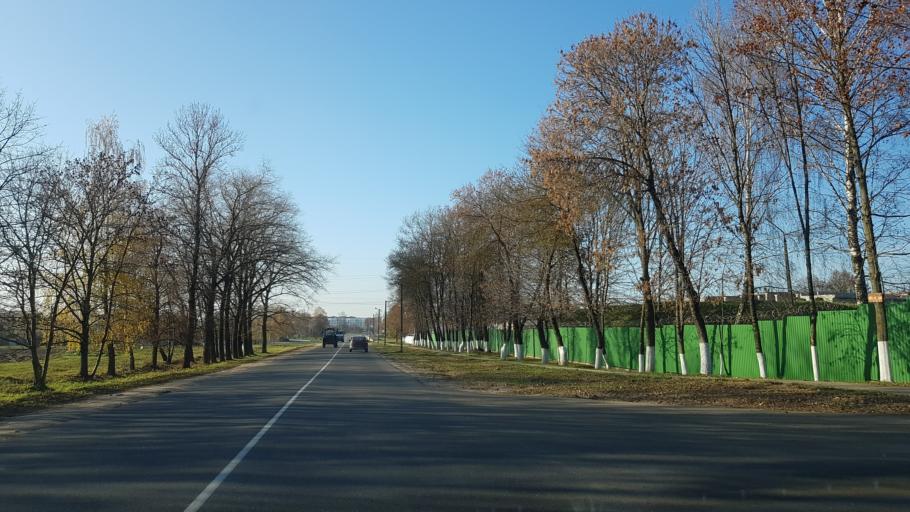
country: BY
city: Fanipol
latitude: 53.7354
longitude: 27.3277
